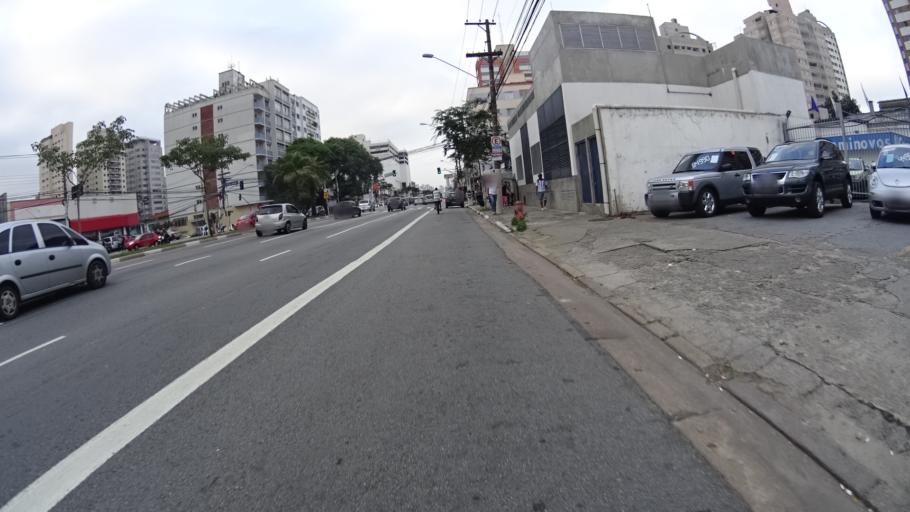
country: BR
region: Sao Paulo
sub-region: Sao Paulo
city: Sao Paulo
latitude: -23.6022
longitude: -46.6365
